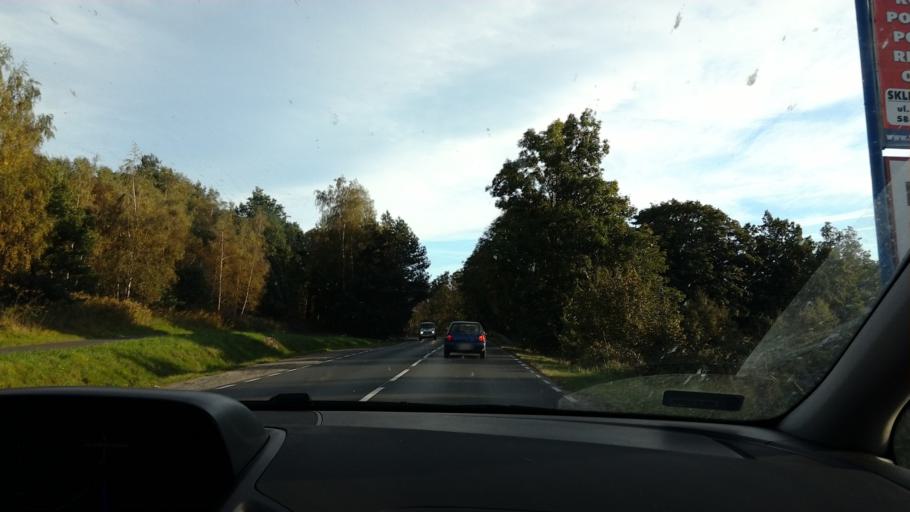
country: PL
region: Lower Silesian Voivodeship
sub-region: Jelenia Gora
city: Jelenia Gora
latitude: 50.8756
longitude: 15.7590
